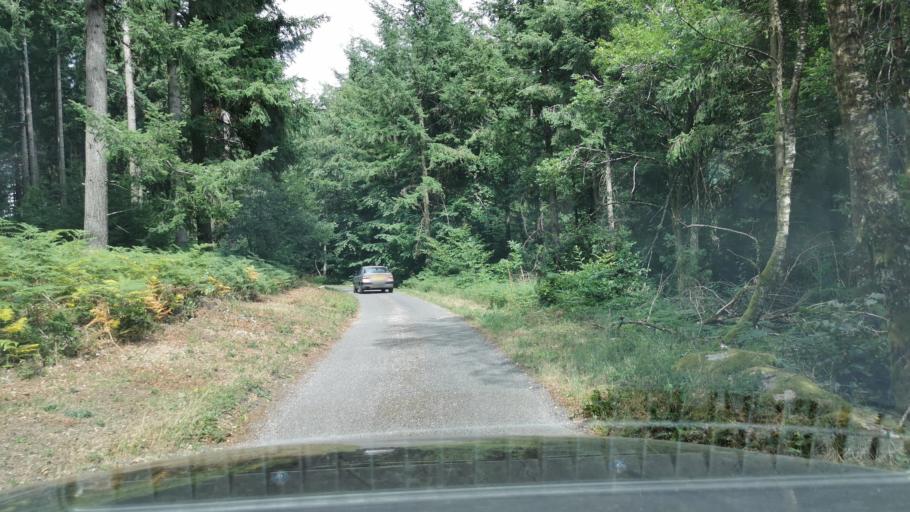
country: FR
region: Bourgogne
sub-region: Departement de Saone-et-Loire
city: Marmagne
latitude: 46.8044
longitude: 4.2755
